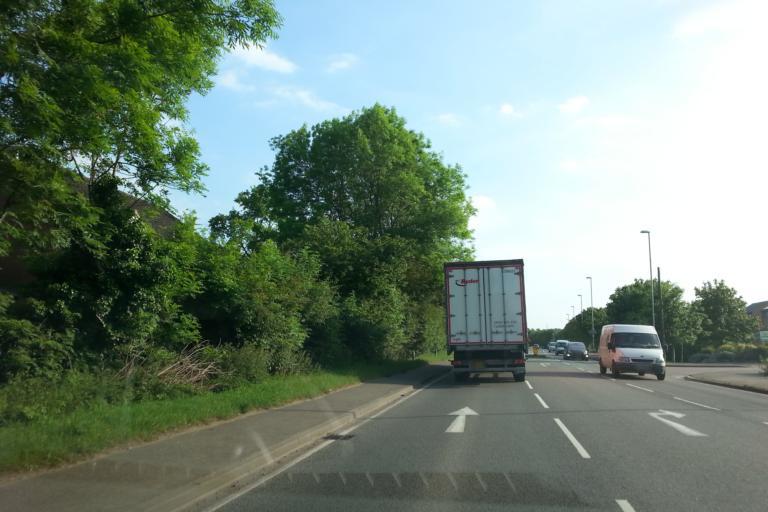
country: GB
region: England
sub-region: Cambridgeshire
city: Hemingford Grey
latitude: 52.3145
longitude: -0.0828
